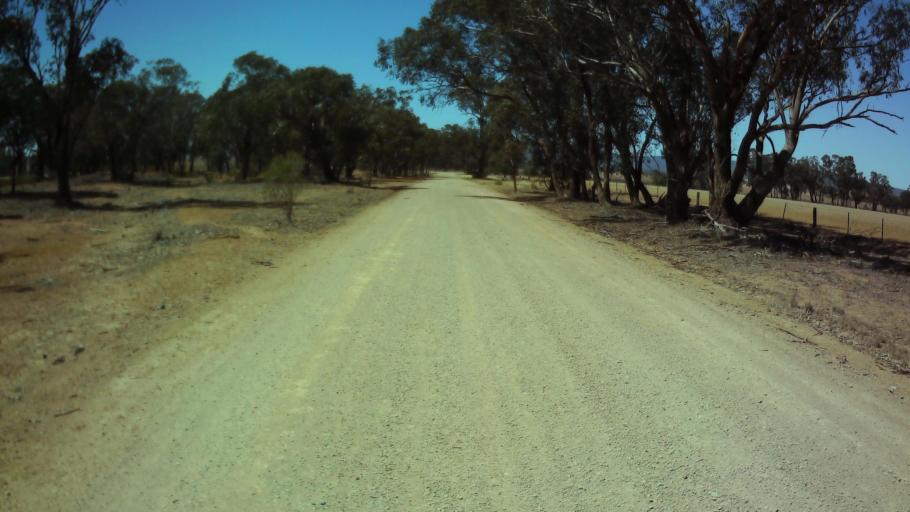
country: AU
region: New South Wales
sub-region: Weddin
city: Grenfell
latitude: -33.8676
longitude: 148.0878
